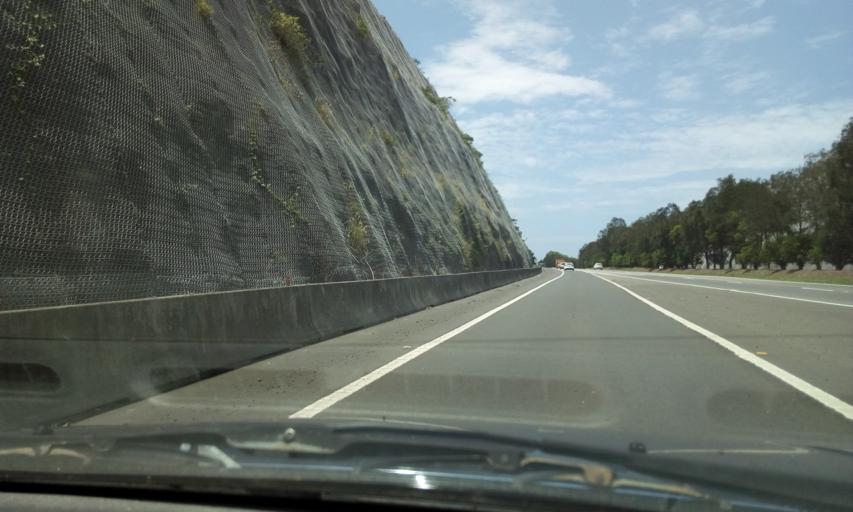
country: AU
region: New South Wales
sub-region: Wollongong
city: Berkeley
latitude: -34.4709
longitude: 150.8349
